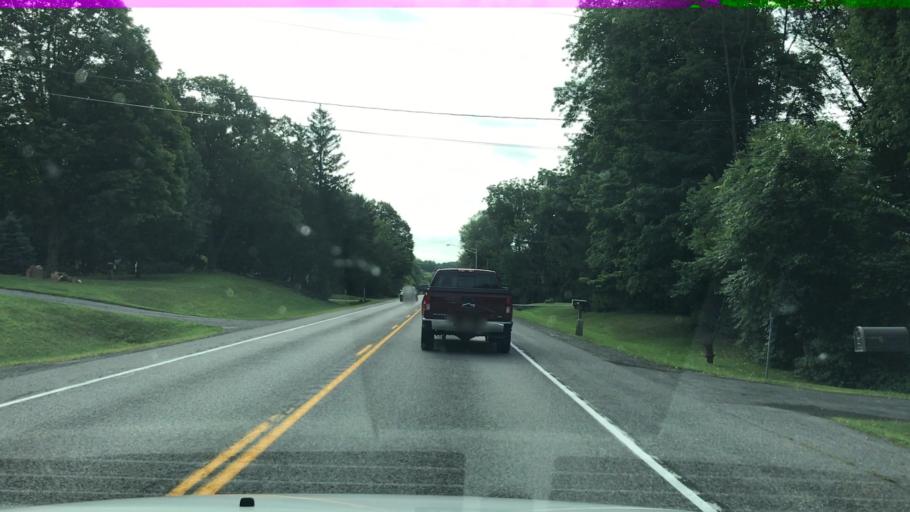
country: US
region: New York
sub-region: Erie County
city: Alden
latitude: 42.8481
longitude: -78.4801
